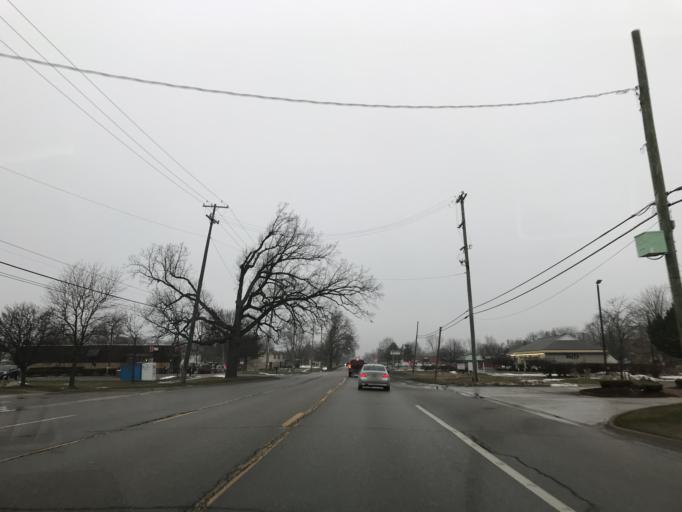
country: US
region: Michigan
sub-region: Oakland County
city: South Lyon
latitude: 42.4477
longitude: -83.6504
